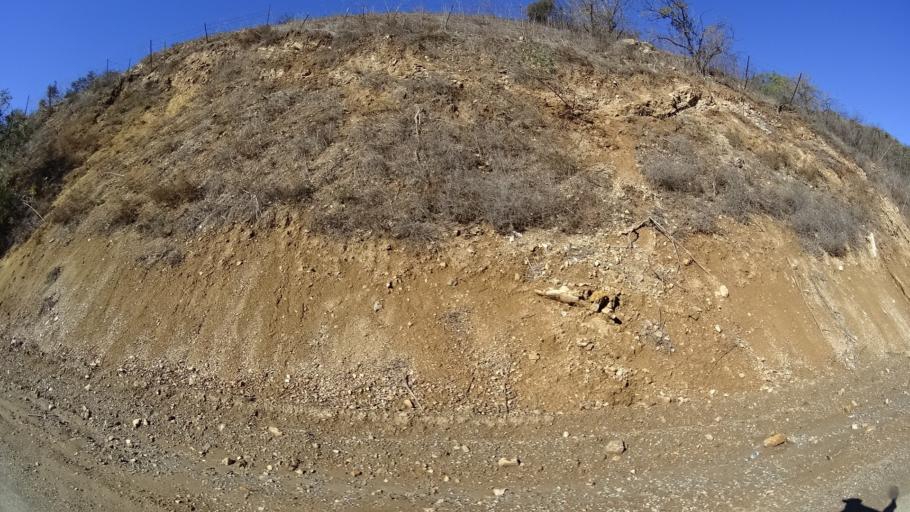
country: US
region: California
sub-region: Los Angeles County
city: Rowland Heights
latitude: 33.9506
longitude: -117.8670
